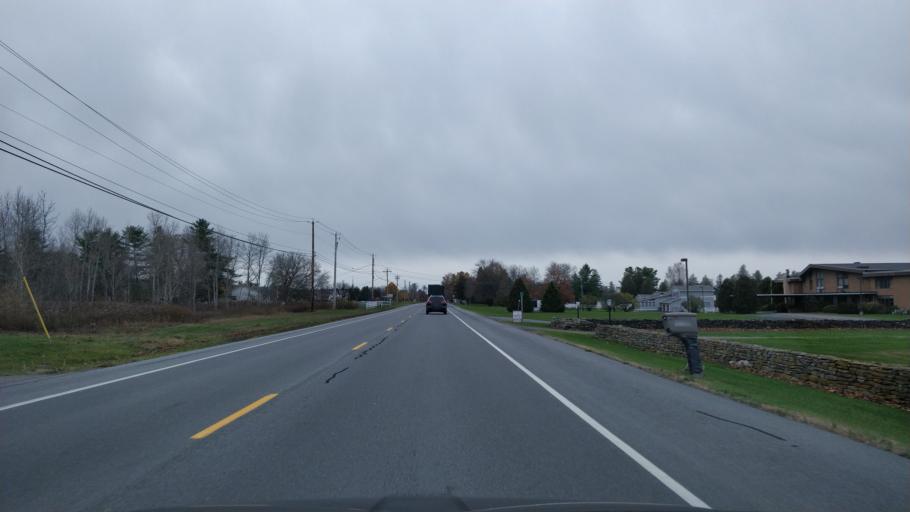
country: CA
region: Ontario
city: Prescott
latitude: 44.6645
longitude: -75.5395
